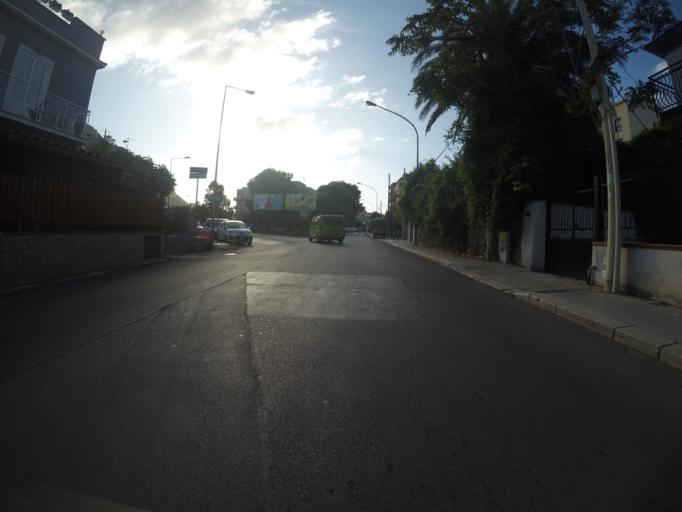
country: IT
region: Sicily
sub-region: Palermo
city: Isola delle Femmine
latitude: 38.1951
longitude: 13.2809
